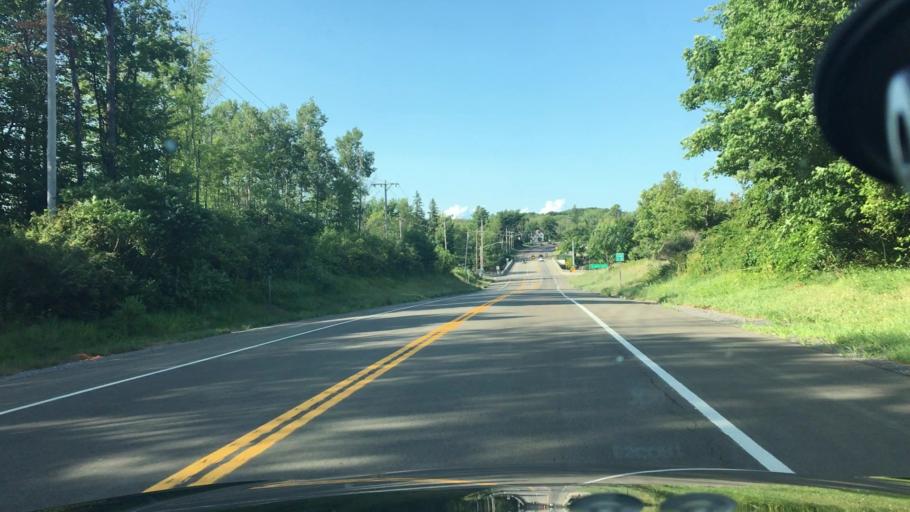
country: US
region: New York
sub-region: Erie County
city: Eden
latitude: 42.6932
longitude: -78.9379
